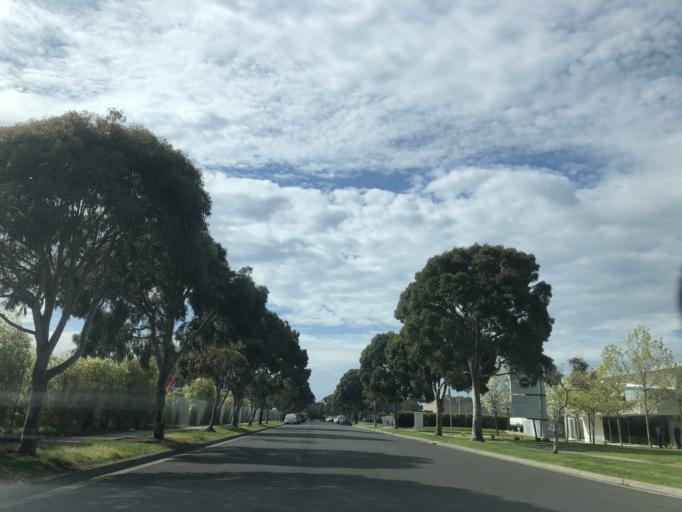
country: AU
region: Victoria
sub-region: Monash
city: Notting Hill
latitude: -37.9211
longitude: 145.1548
